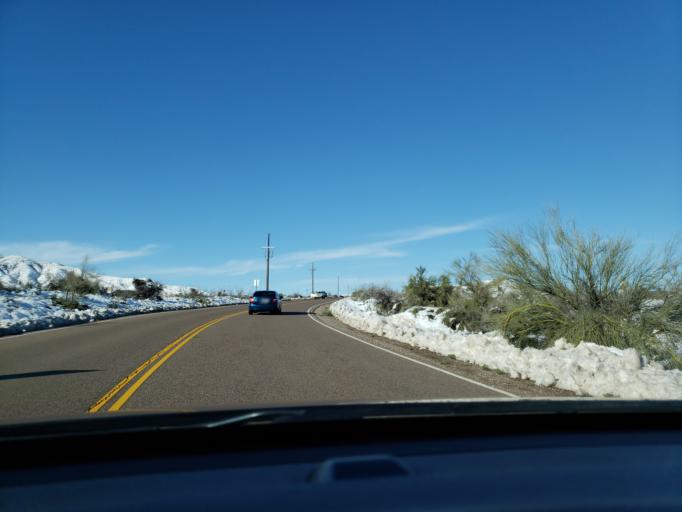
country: US
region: Arizona
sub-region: Maricopa County
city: Carefree
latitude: 33.8593
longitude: -111.8309
